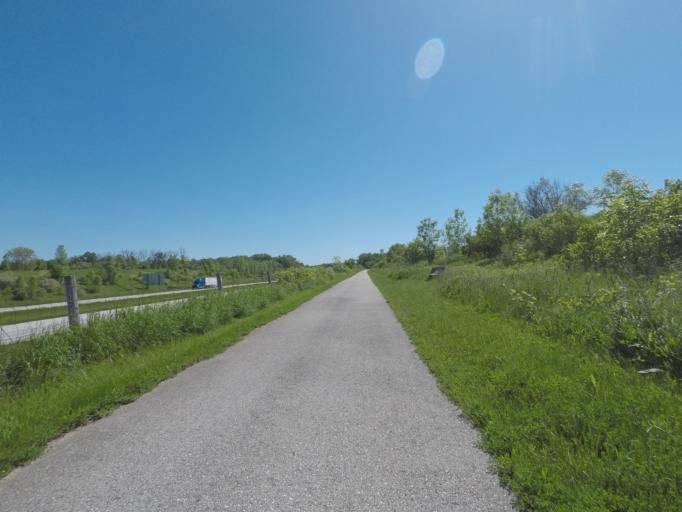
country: US
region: Wisconsin
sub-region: Sheboygan County
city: Kohler
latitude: 43.7508
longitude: -87.7973
